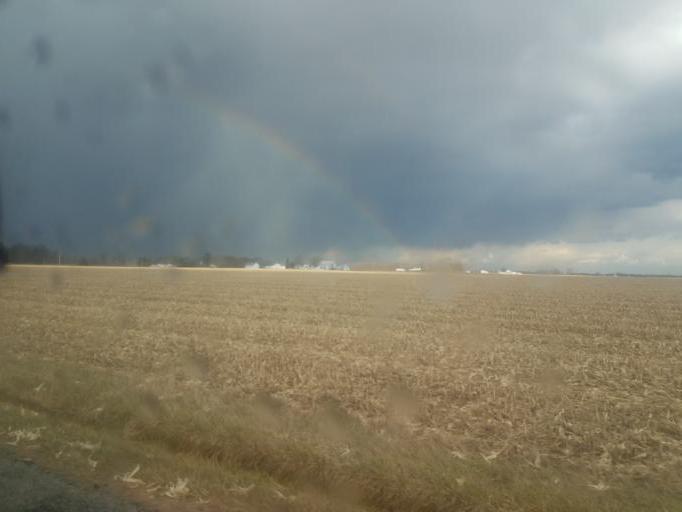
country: US
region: Ohio
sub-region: Marion County
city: Prospect
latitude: 40.4799
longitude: -83.1176
